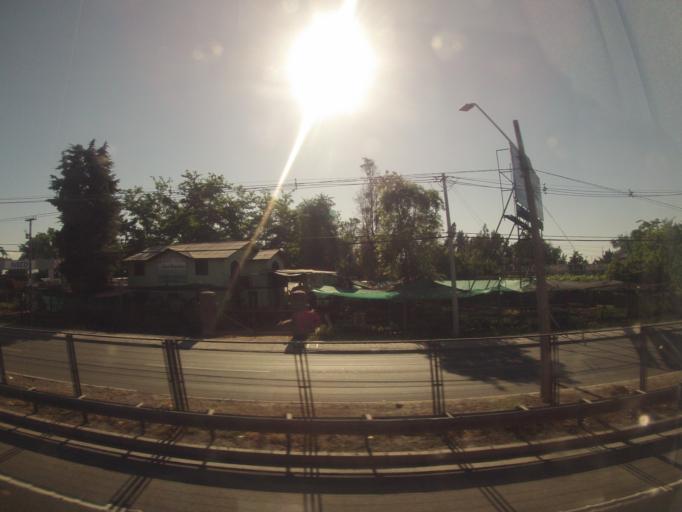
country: CL
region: Santiago Metropolitan
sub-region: Provincia de Maipo
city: San Bernardo
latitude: -33.6416
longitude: -70.7120
